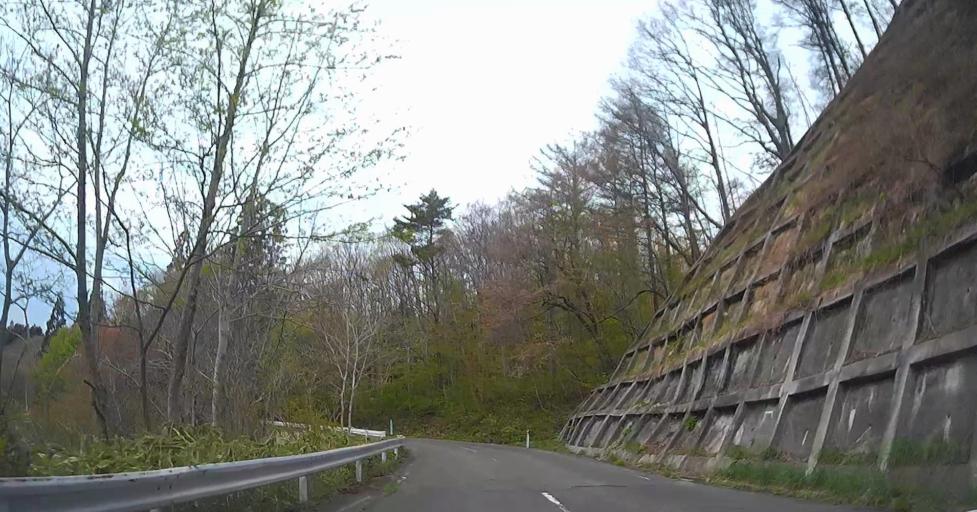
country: JP
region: Aomori
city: Goshogawara
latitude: 40.9038
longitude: 140.5254
